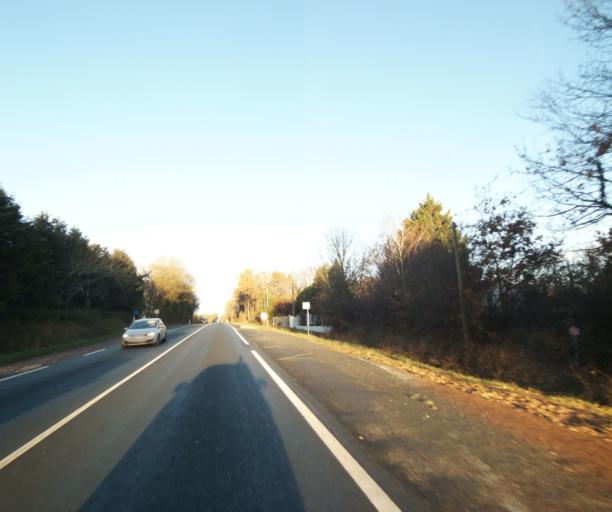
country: FR
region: Poitou-Charentes
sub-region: Departement de la Charente-Maritime
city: Saintes
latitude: 45.7610
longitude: -0.6682
